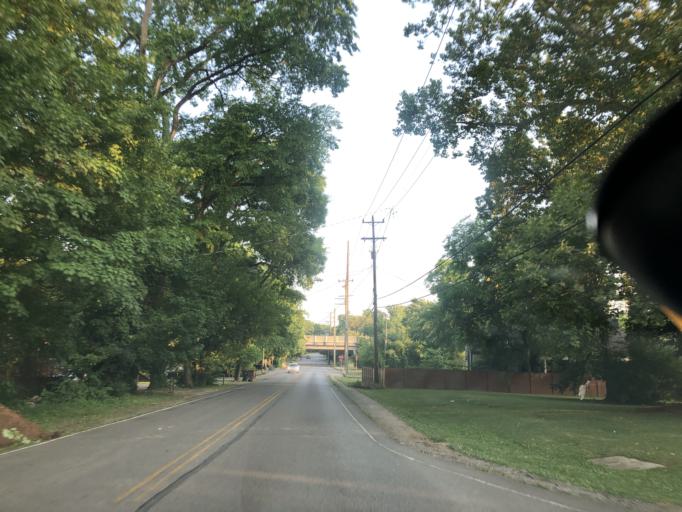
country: US
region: Tennessee
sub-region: Davidson County
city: Oak Hill
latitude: 36.1179
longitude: -86.7872
